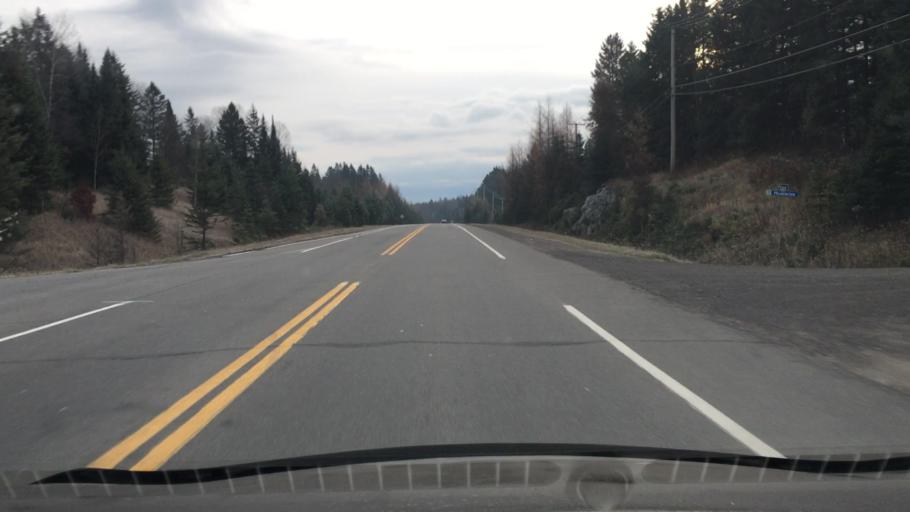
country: CA
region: Quebec
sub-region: Laurentides
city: Saint-Sauveur
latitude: 45.9028
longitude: -74.2326
